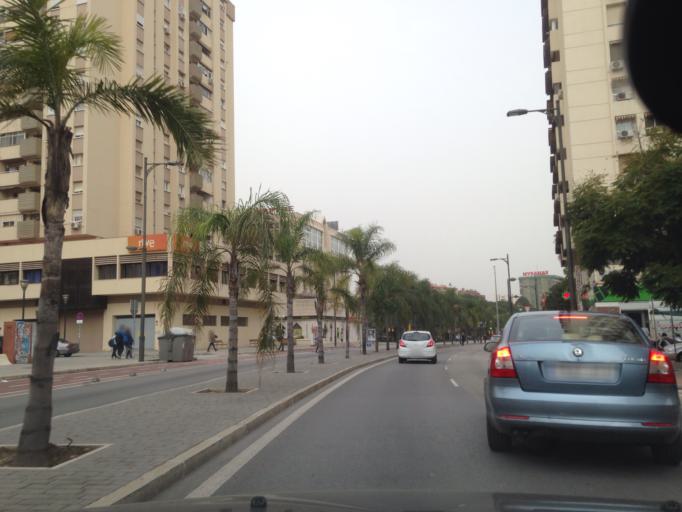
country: ES
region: Andalusia
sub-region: Provincia de Malaga
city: Malaga
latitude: 36.7154
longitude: -4.4390
